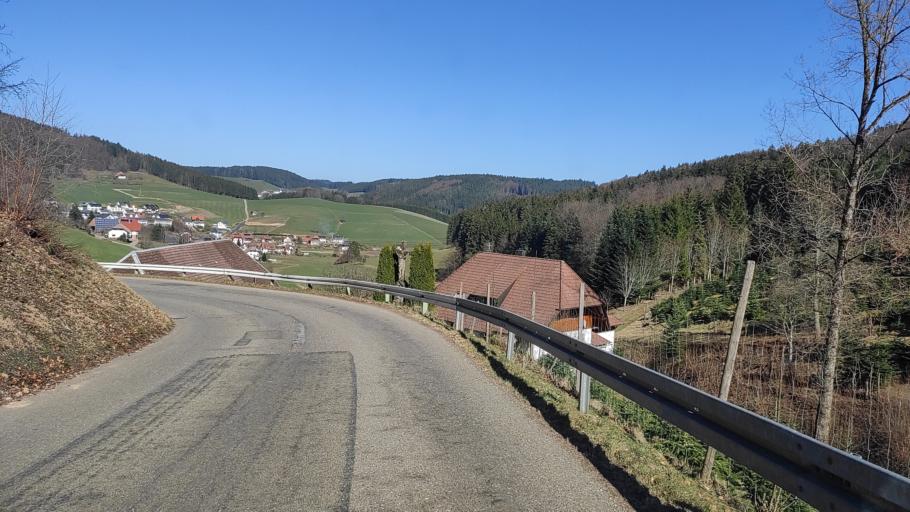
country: DE
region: Baden-Wuerttemberg
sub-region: Freiburg Region
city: Elzach
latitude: 48.1872
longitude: 8.0297
